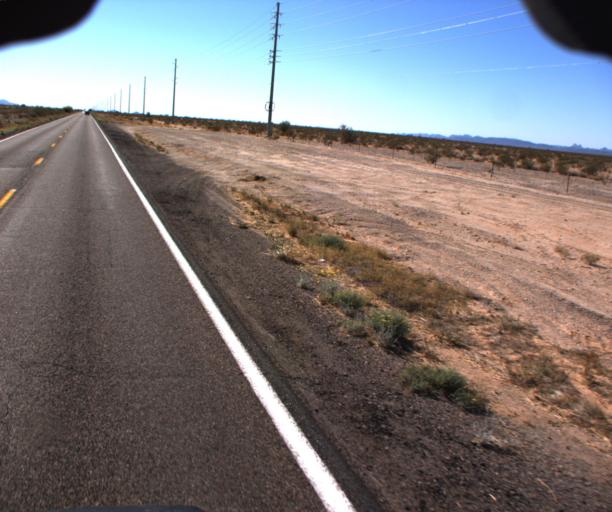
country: US
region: Arizona
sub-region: La Paz County
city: Quartzsite
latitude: 33.8969
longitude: -113.9682
